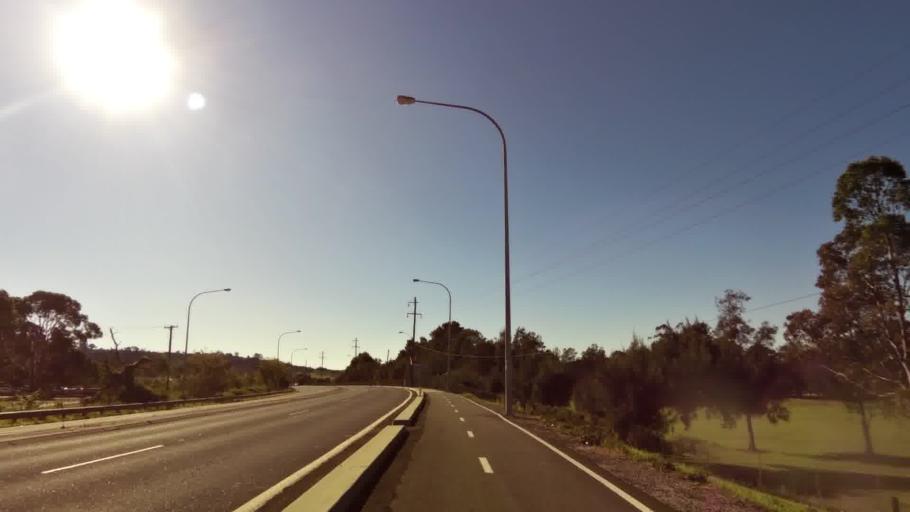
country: AU
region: New South Wales
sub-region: Wollongong
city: Koonawarra
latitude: -34.4743
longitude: 150.8129
